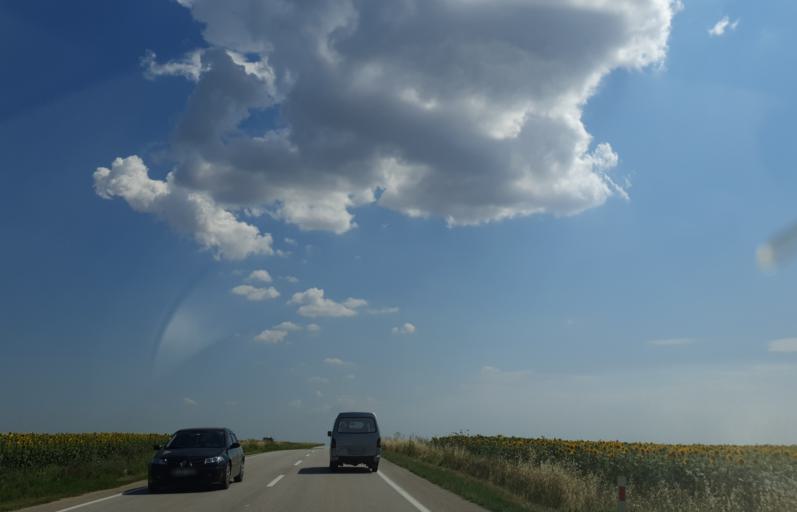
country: TR
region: Kirklareli
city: Buyukkaristiran
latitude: 41.4066
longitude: 27.5761
